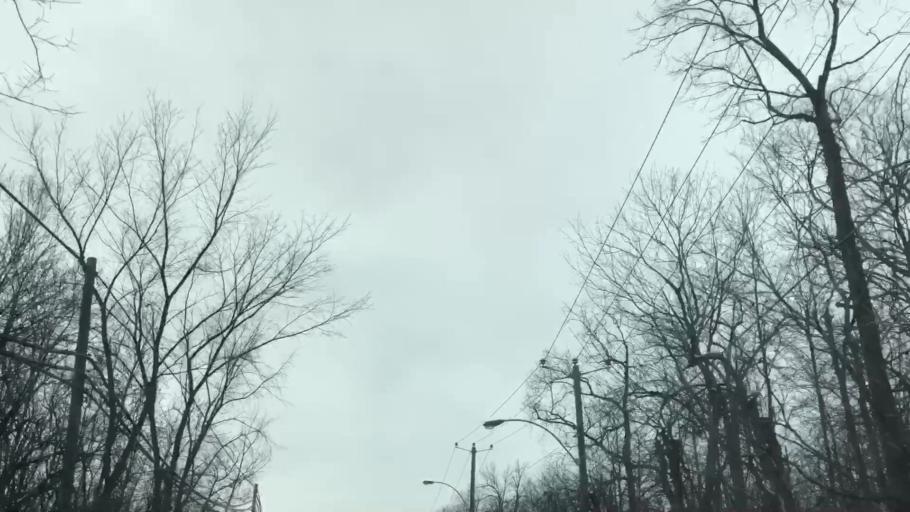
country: CA
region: Quebec
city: Dorval
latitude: 45.5092
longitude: -73.7572
